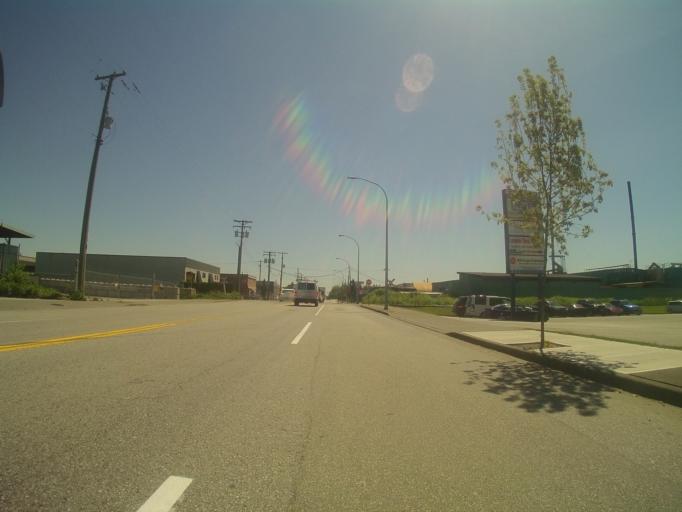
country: CA
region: British Columbia
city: Richmond
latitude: 49.1951
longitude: -123.0915
